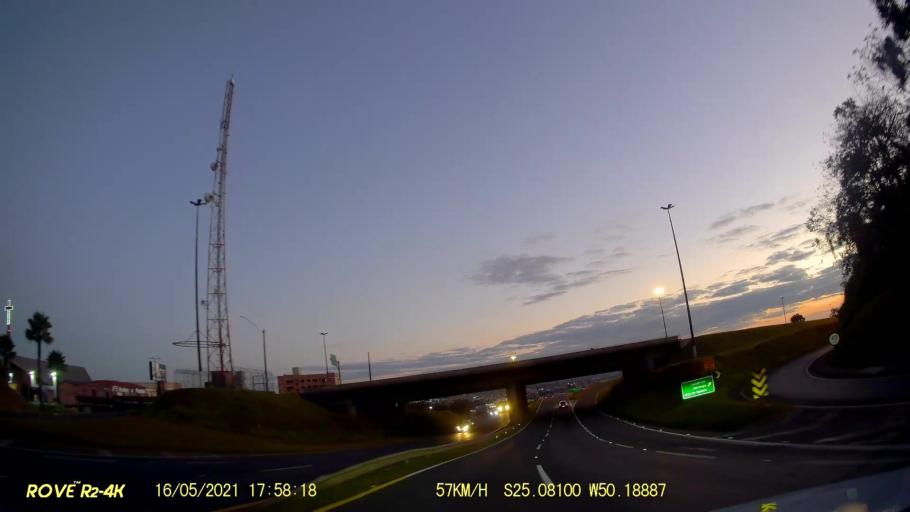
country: BR
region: Parana
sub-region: Ponta Grossa
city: Ponta Grossa
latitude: -25.0807
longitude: -50.1892
